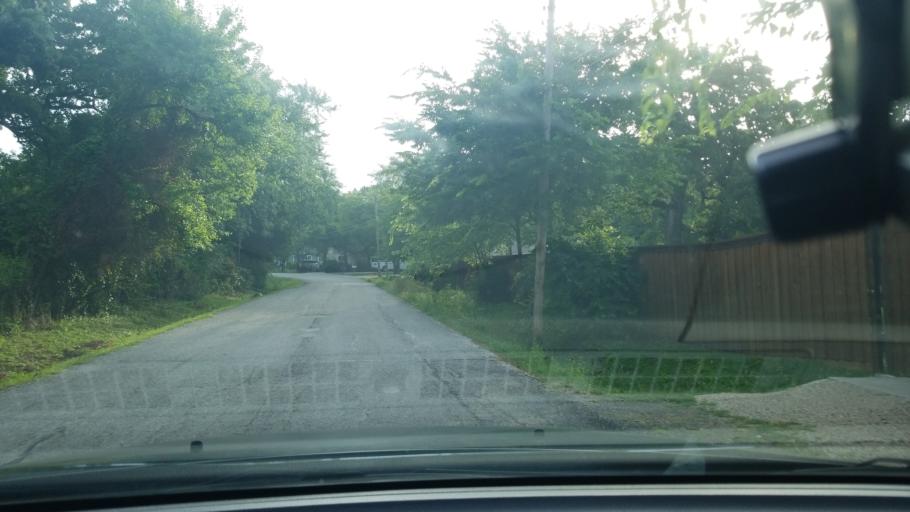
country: US
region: Texas
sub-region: Dallas County
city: Balch Springs
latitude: 32.7586
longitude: -96.6416
